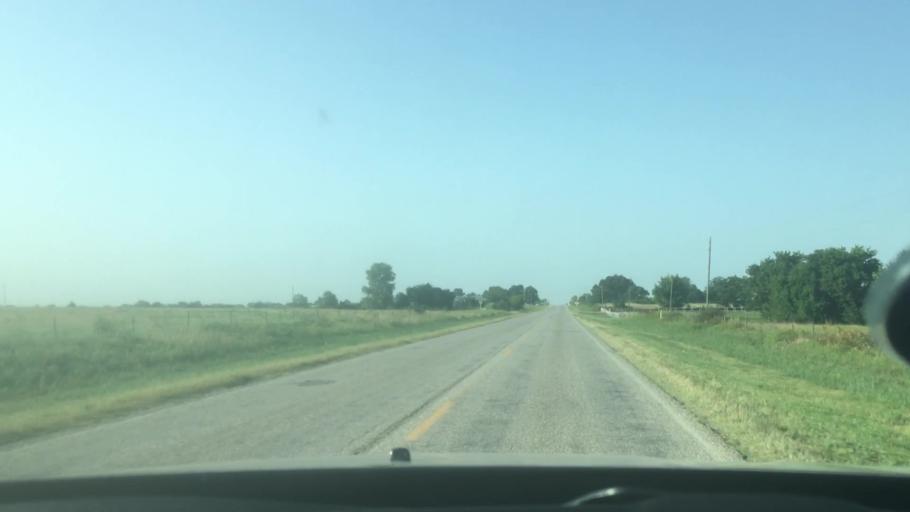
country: US
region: Oklahoma
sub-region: Johnston County
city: Tishomingo
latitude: 34.2835
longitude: -96.4248
